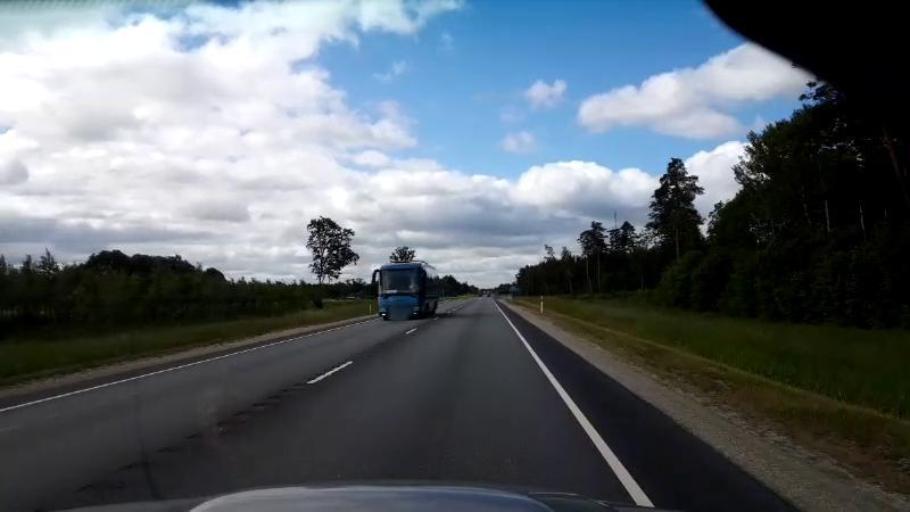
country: EE
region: Harju
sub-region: Nissi vald
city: Riisipere
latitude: 59.0624
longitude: 24.4490
